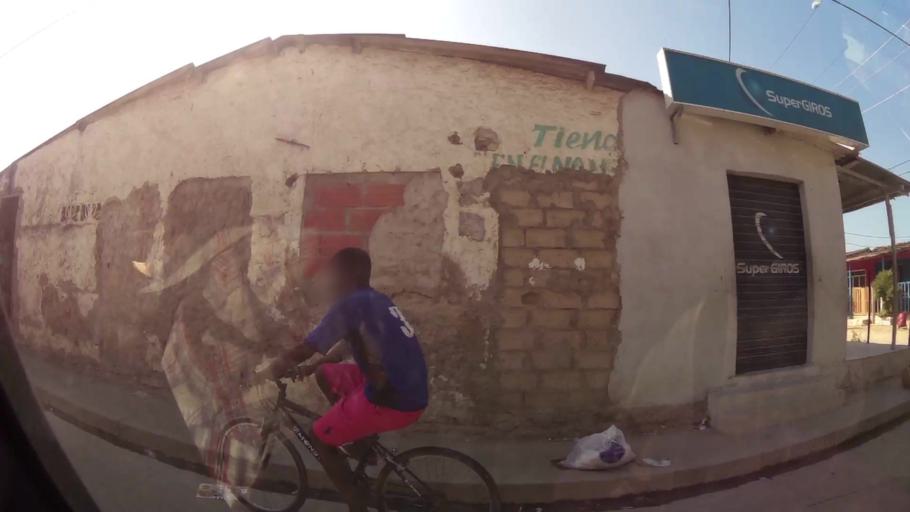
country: CO
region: Bolivar
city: Cartagena
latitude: 10.4115
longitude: -75.5122
